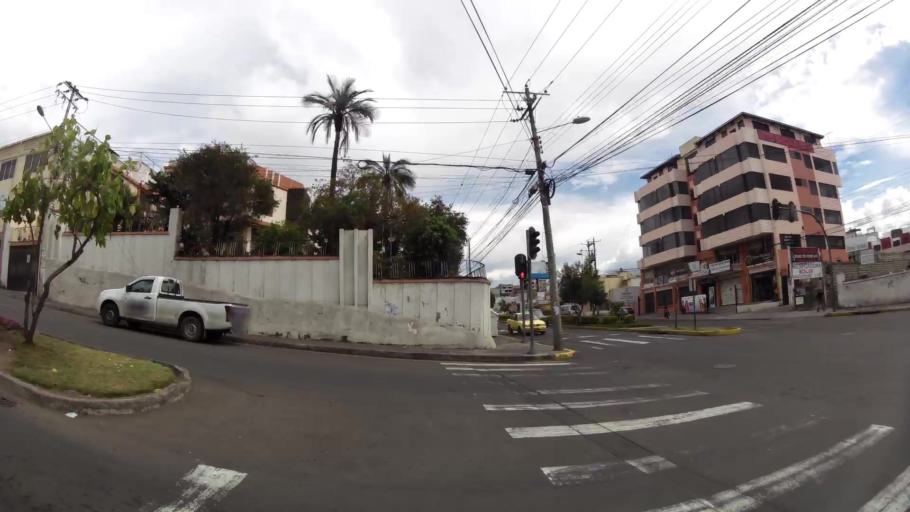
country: EC
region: Tungurahua
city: Ambato
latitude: -1.2559
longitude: -78.6319
